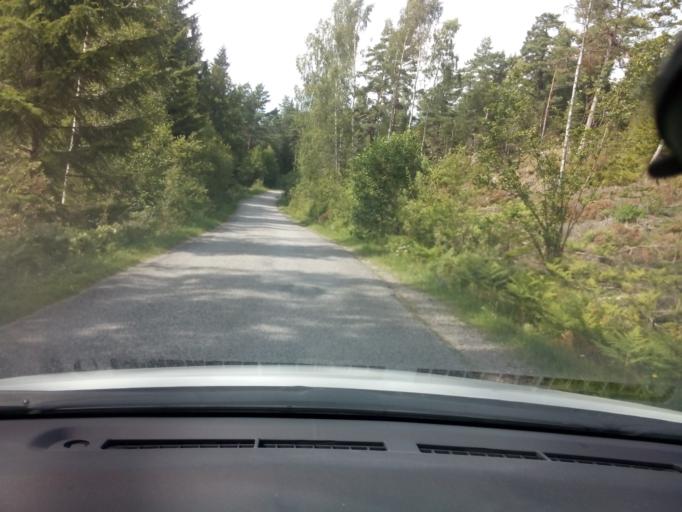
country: SE
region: Soedermanland
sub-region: Trosa Kommun
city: Trosa
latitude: 58.7554
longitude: 17.3723
